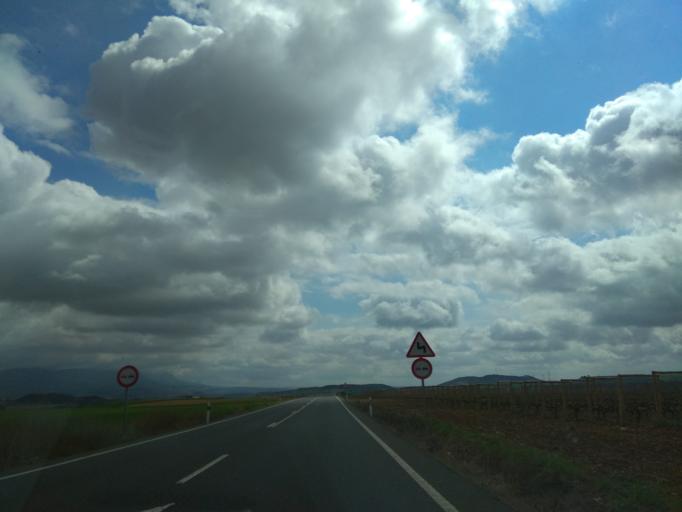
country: ES
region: La Rioja
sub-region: Provincia de La Rioja
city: Rodezno
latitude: 42.5435
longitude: -2.8569
